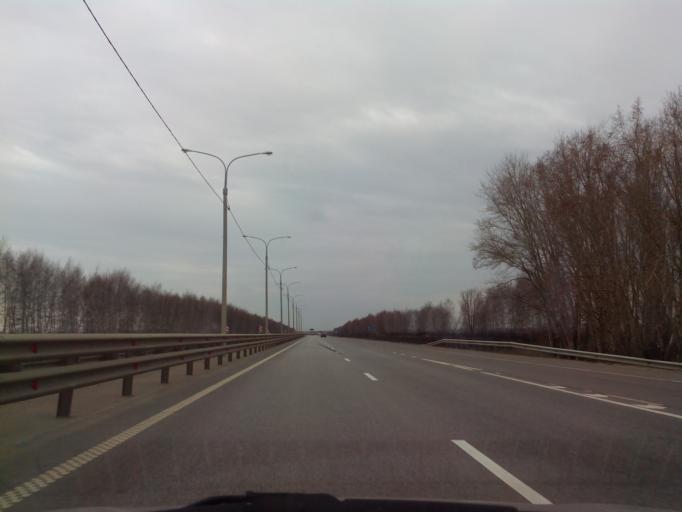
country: RU
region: Tambov
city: Zavoronezhskoye
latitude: 52.8483
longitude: 40.8104
